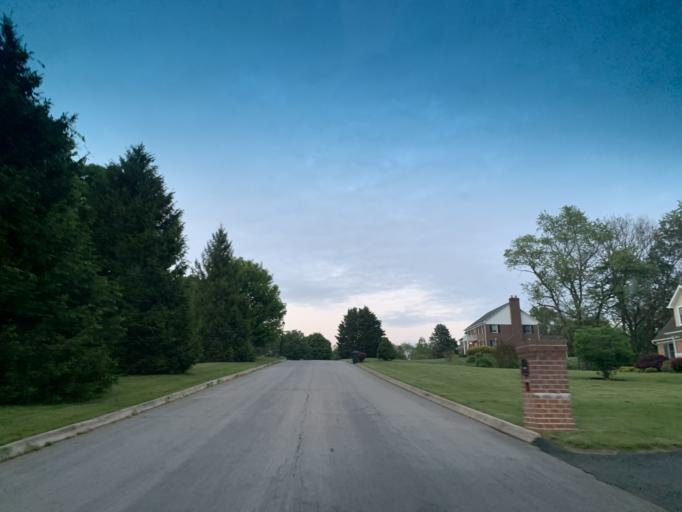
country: US
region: Maryland
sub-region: Harford County
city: South Bel Air
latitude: 39.5891
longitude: -76.2666
